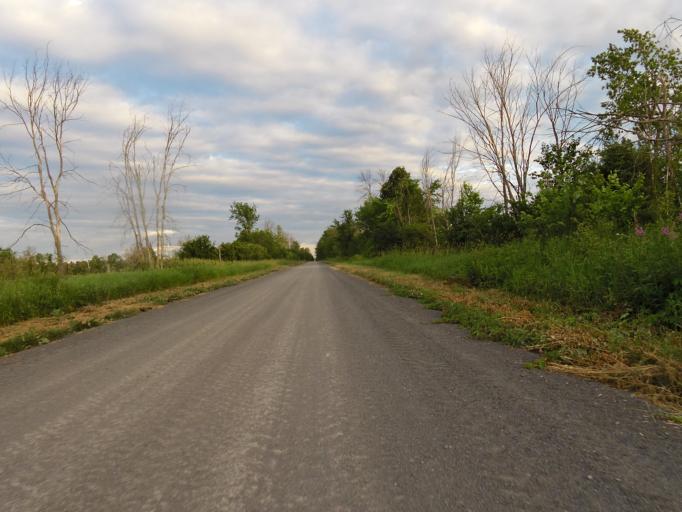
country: CA
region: Ontario
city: Arnprior
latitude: 45.3434
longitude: -76.2996
